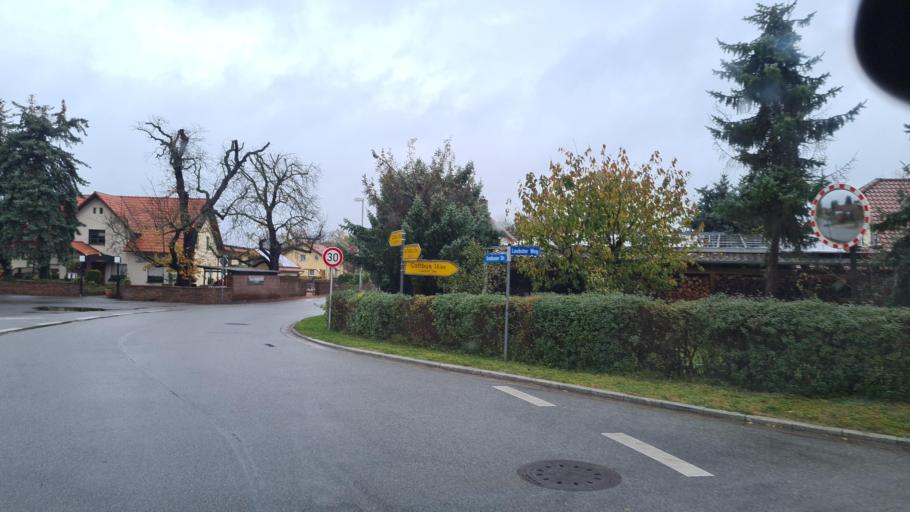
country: DE
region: Brandenburg
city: Drebkau
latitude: 51.6787
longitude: 14.2021
